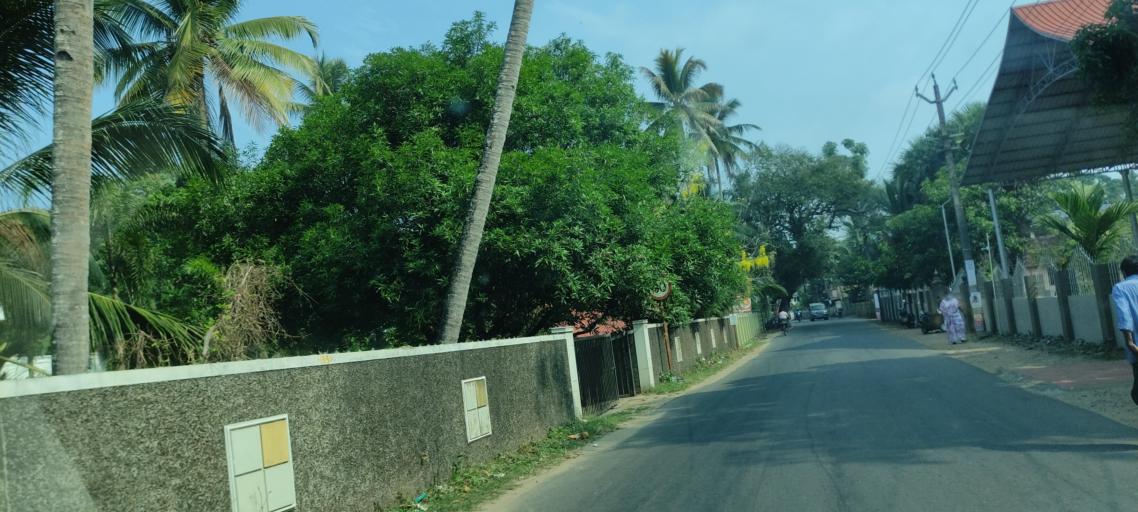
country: IN
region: Kerala
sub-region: Alappuzha
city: Kutiatodu
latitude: 9.7804
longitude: 76.3045
